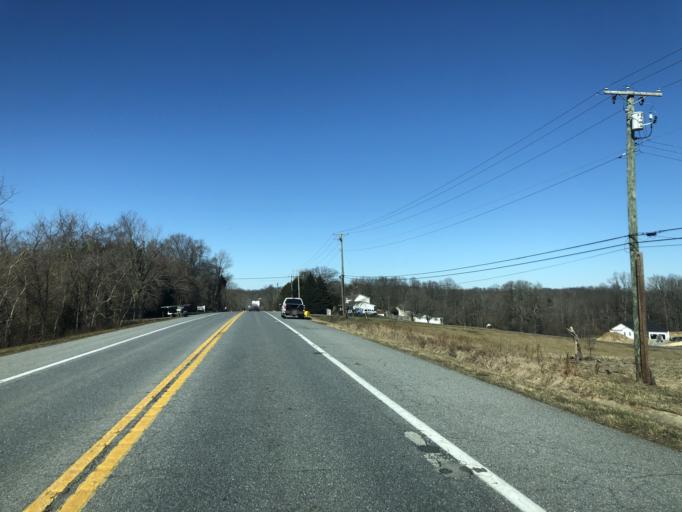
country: US
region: Maryland
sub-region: Calvert County
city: Dunkirk
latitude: 38.7870
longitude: -76.6419
